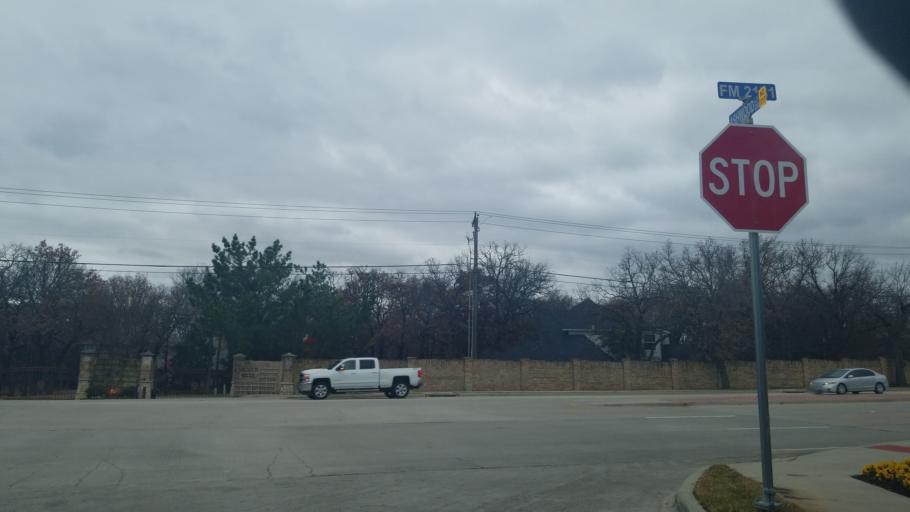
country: US
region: Texas
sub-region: Denton County
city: Corinth
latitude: 33.1323
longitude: -97.0825
